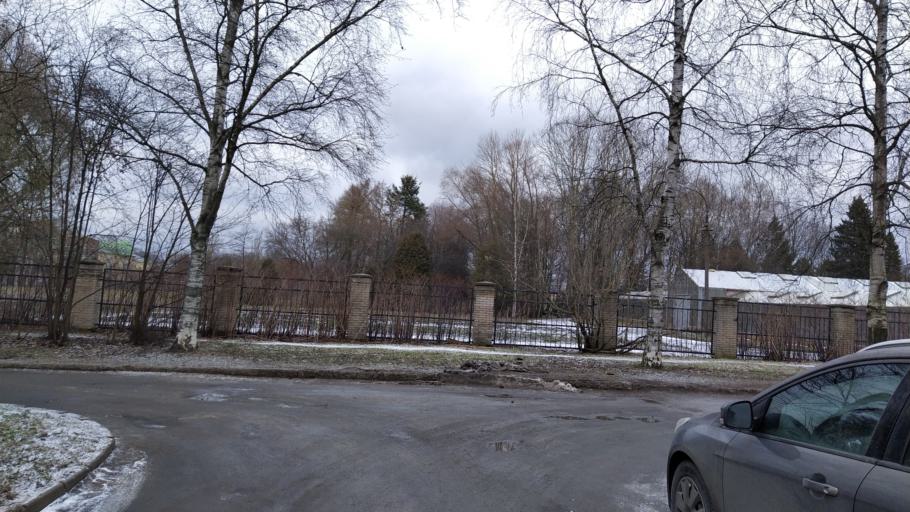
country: RU
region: St.-Petersburg
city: Pushkin
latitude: 59.7231
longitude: 30.4173
